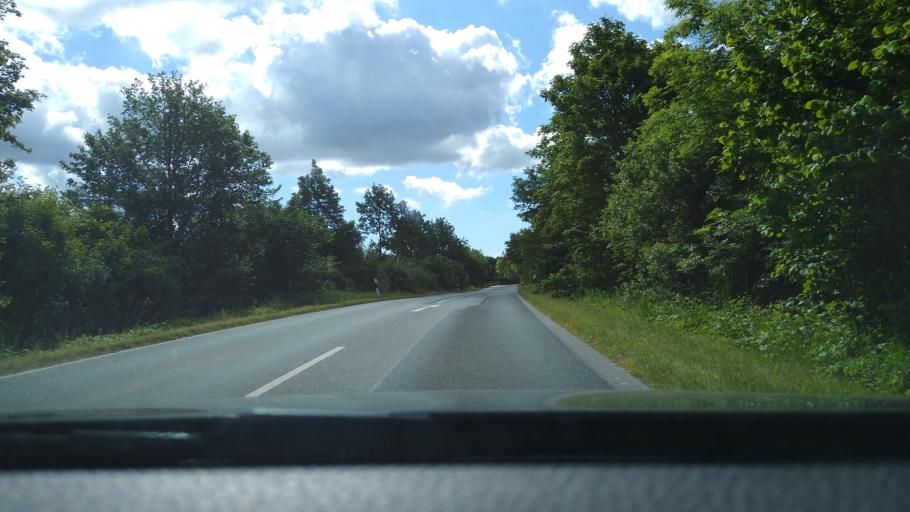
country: DE
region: Schleswig-Holstein
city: Riepsdorf
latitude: 54.2097
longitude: 10.9488
